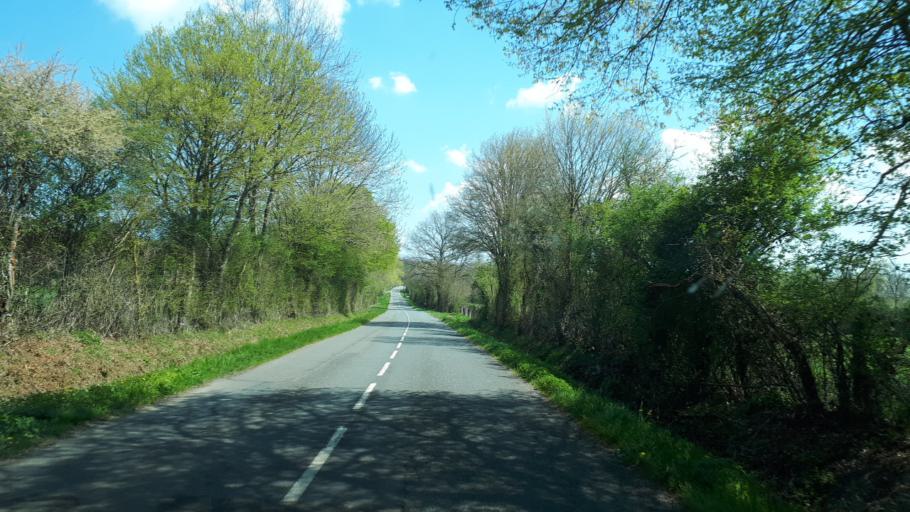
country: FR
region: Centre
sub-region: Departement du Cher
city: Sancerre
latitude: 47.3039
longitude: 2.7072
